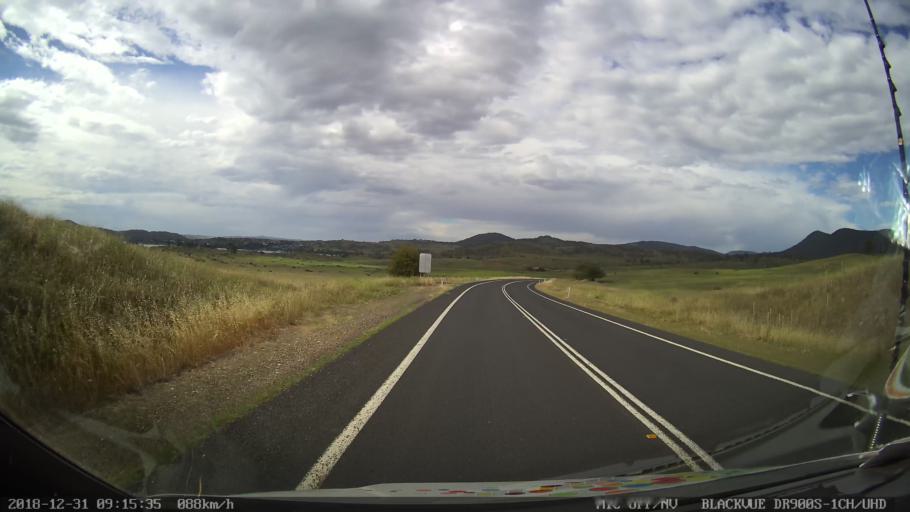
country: AU
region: New South Wales
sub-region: Snowy River
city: Jindabyne
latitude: -36.3871
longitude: 148.5992
